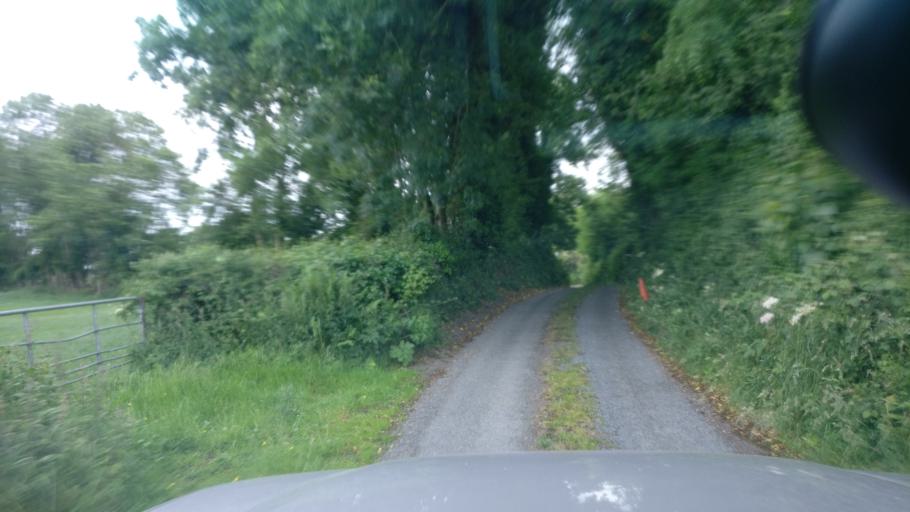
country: IE
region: Connaught
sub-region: County Galway
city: Ballinasloe
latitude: 53.3025
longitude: -8.2872
